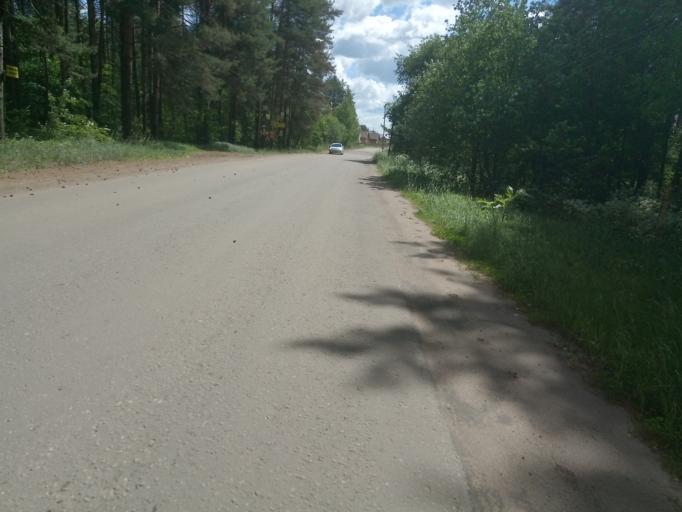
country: RU
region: Jaroslavl
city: Yaroslavl
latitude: 57.6548
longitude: 39.9846
